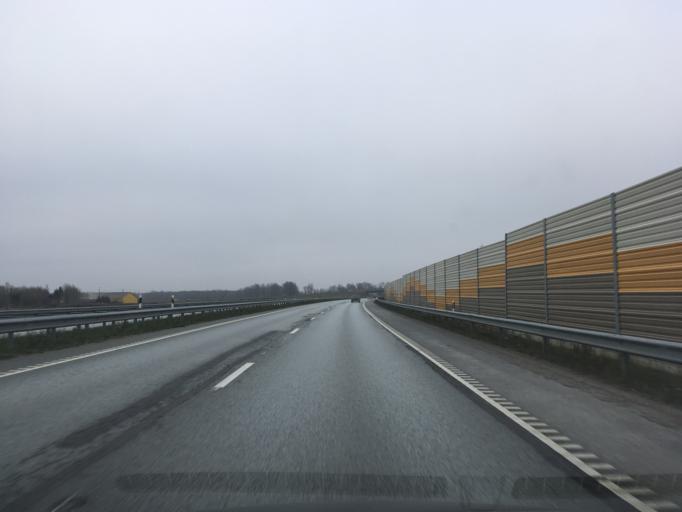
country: EE
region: Ida-Virumaa
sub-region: Johvi vald
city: Johvi
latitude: 59.3795
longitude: 27.3722
